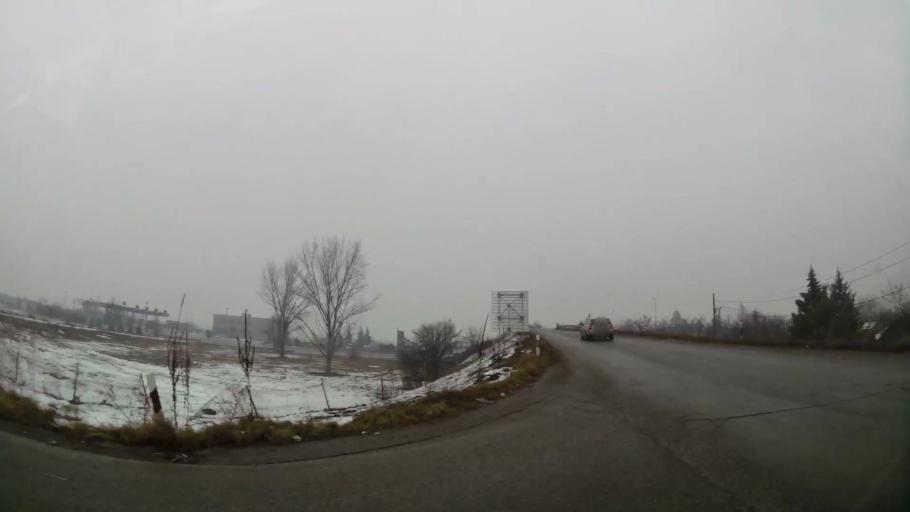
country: MK
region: Petrovec
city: Petrovec
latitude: 41.9405
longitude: 21.6203
